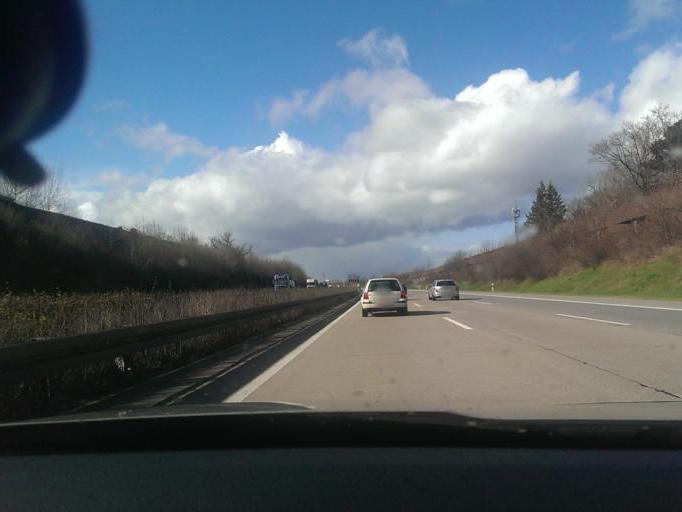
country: DE
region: Lower Saxony
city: Isernhagen Farster Bauerschaft
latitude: 52.4730
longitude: 9.8549
